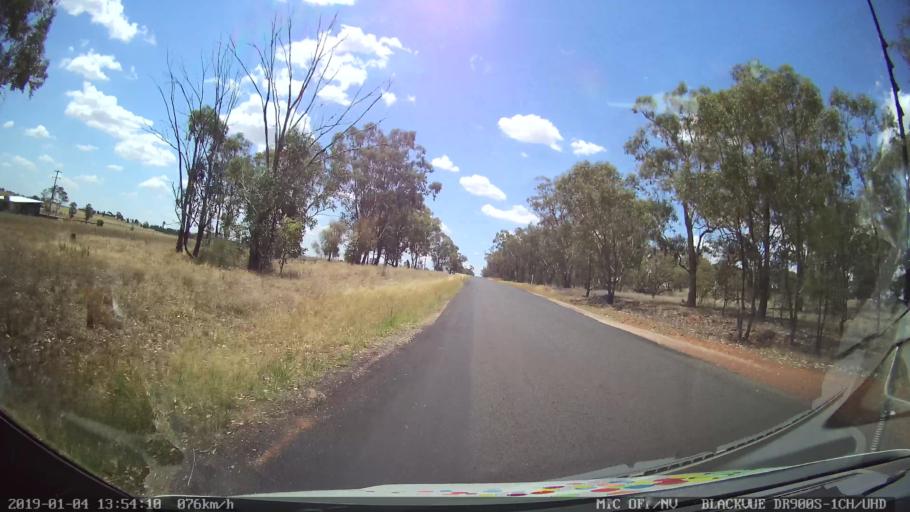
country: AU
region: New South Wales
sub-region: Dubbo Municipality
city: Dubbo
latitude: -32.3758
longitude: 148.5790
